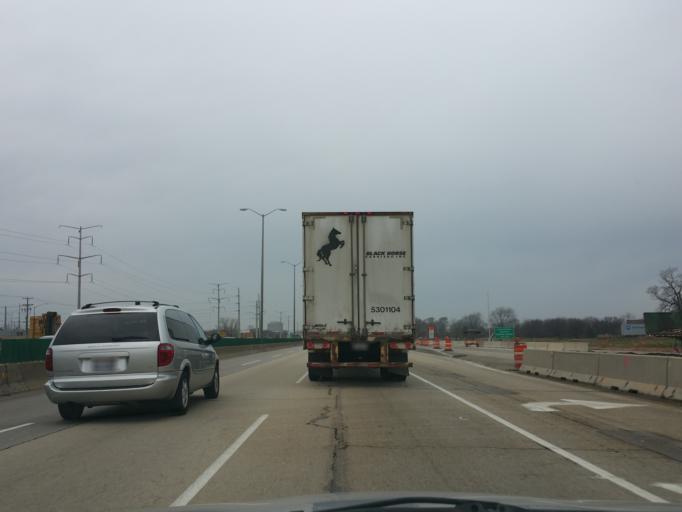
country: US
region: Illinois
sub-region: Cook County
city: Hoffman Estates
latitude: 42.0604
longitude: -88.0505
